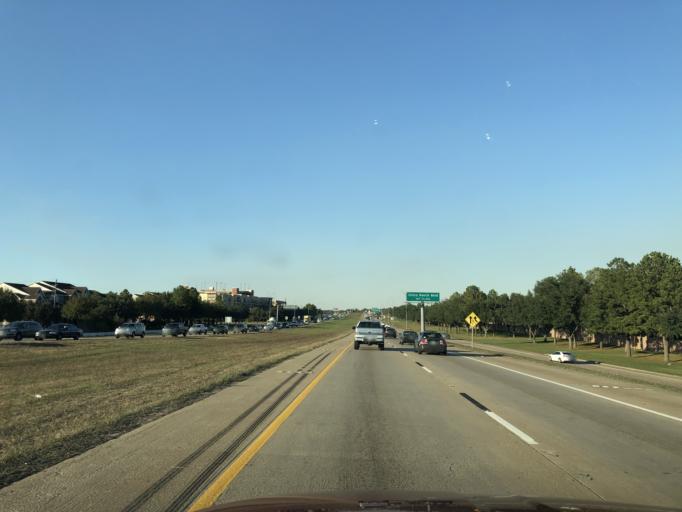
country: US
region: Texas
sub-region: Fort Bend County
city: Cinco Ranch
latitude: 29.7351
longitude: -95.7728
